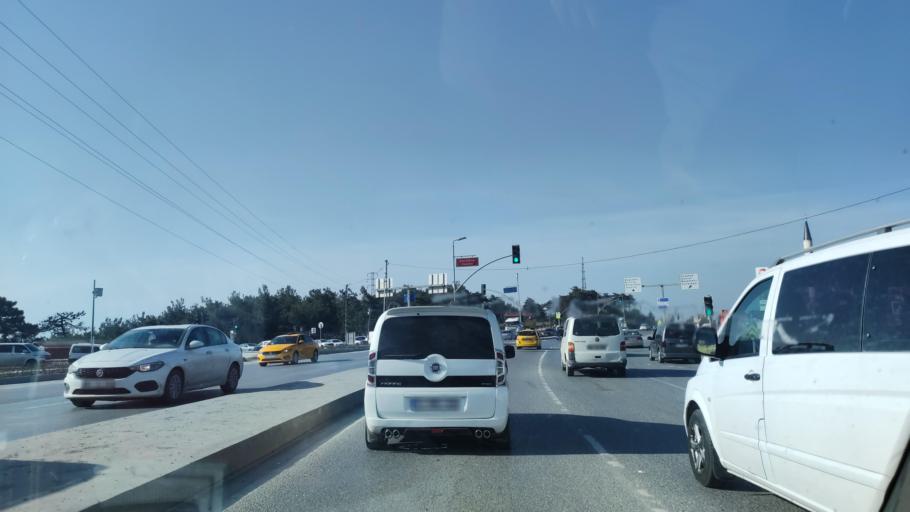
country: TR
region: Istanbul
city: Basaksehir
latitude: 41.1518
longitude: 28.7872
